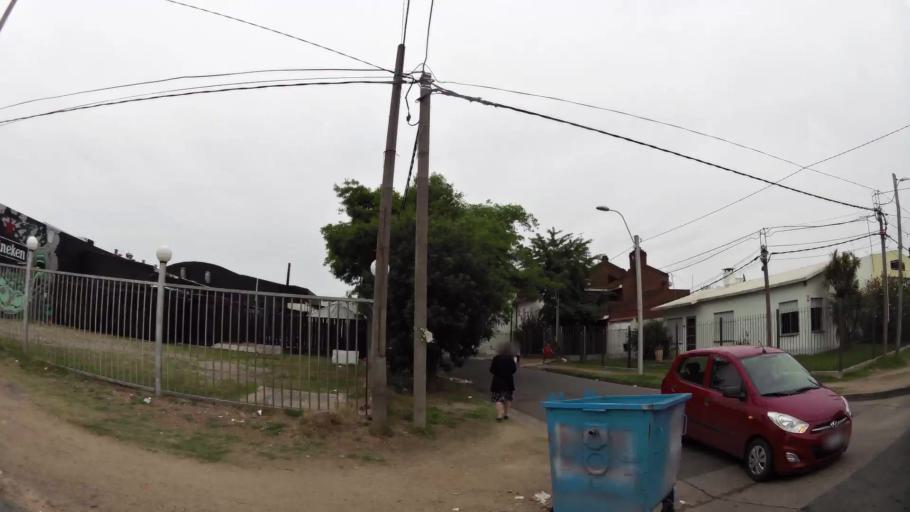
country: UY
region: Canelones
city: Las Piedras
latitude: -34.7273
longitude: -56.2247
